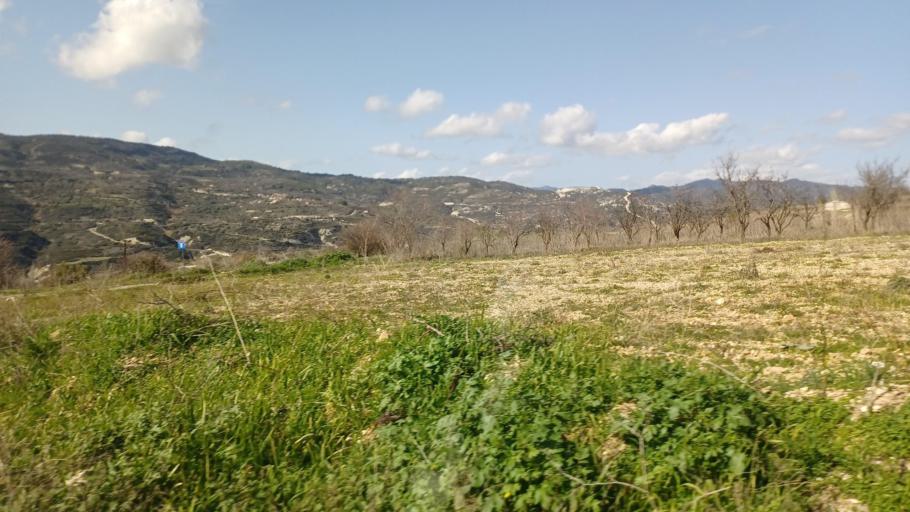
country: CY
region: Limassol
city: Pachna
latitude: 34.8445
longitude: 32.7355
